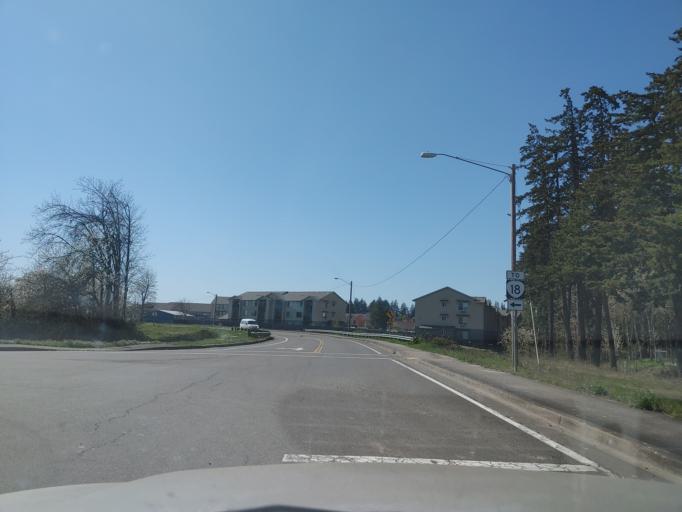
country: US
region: Oregon
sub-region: Yamhill County
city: McMinnville
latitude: 45.2022
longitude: -123.1522
